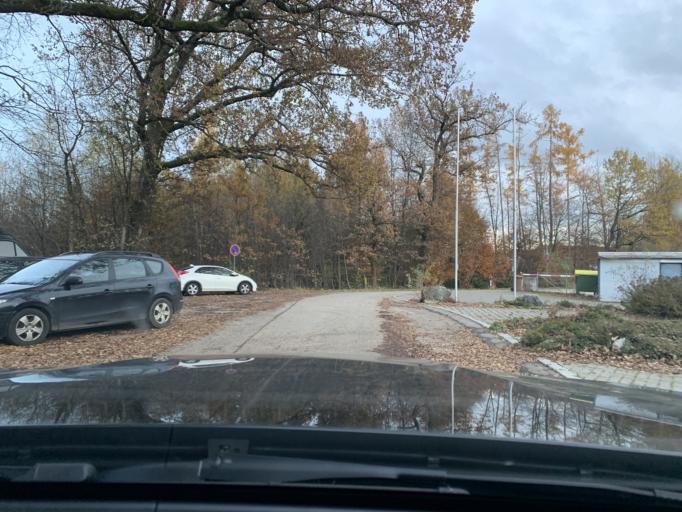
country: DE
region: Bavaria
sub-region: Upper Bavaria
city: Holzkirchen
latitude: 47.8826
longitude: 11.7150
